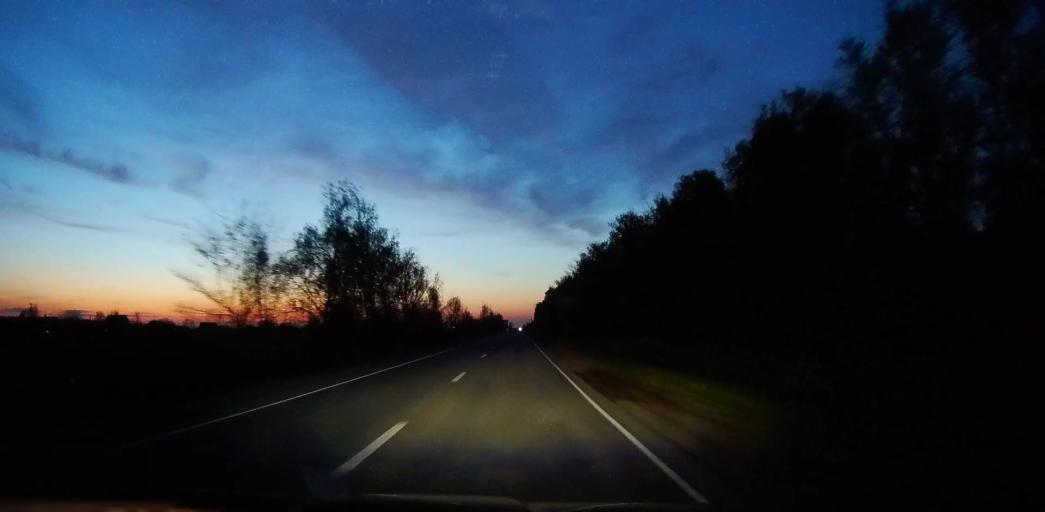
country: RU
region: Moskovskaya
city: Peski
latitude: 55.2348
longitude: 38.7633
